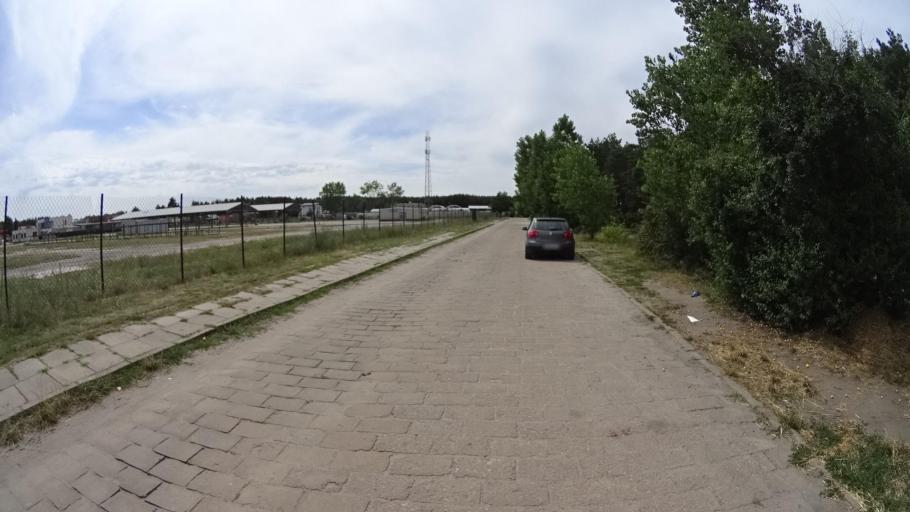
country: PL
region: Masovian Voivodeship
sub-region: Powiat bialobrzeski
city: Bialobrzegi
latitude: 51.6491
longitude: 20.9401
